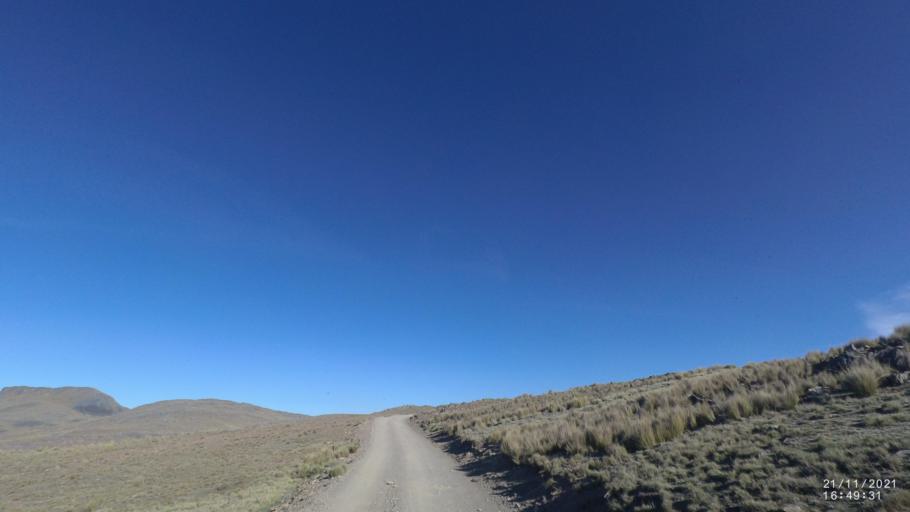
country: BO
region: Cochabamba
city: Cochabamba
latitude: -17.0824
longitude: -66.2534
